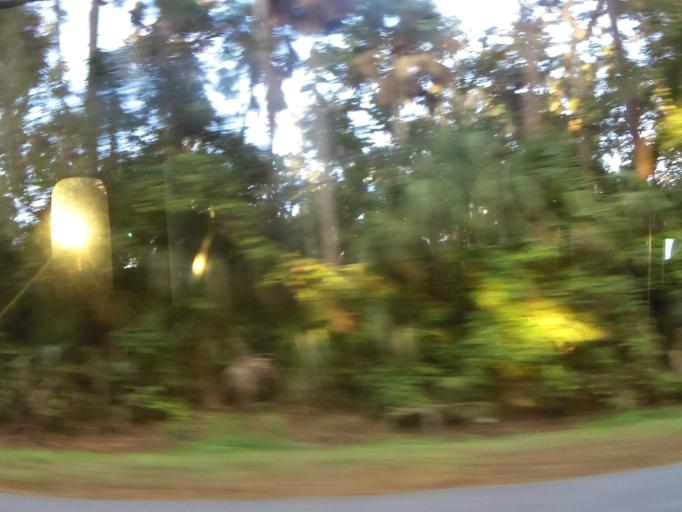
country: US
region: Florida
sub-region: Saint Johns County
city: Palm Valley
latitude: 30.1474
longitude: -81.3913
